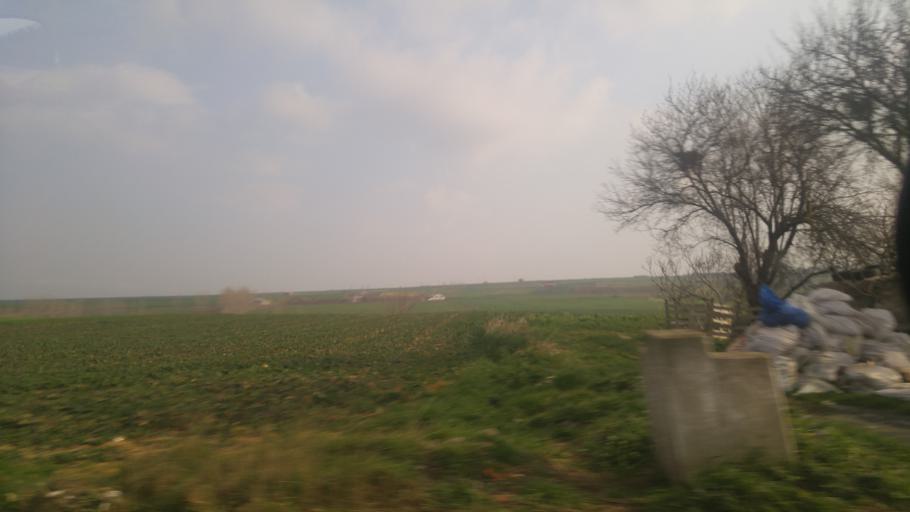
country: TR
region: Istanbul
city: Silivri
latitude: 41.0928
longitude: 28.2745
